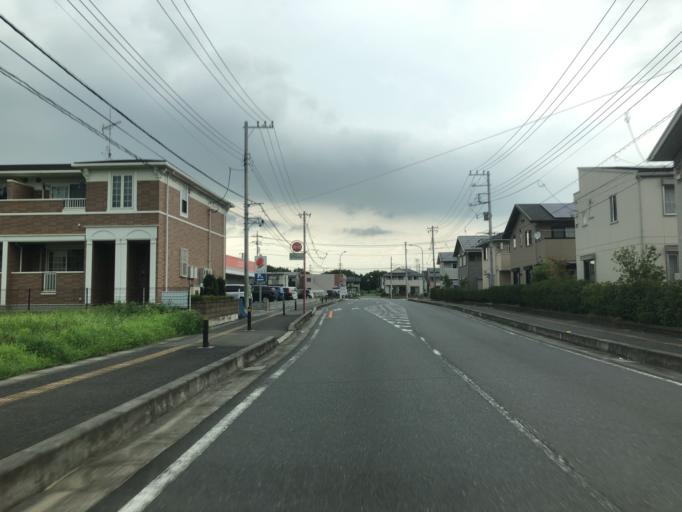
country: JP
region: Saitama
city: Sakado
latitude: 36.0054
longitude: 139.4061
